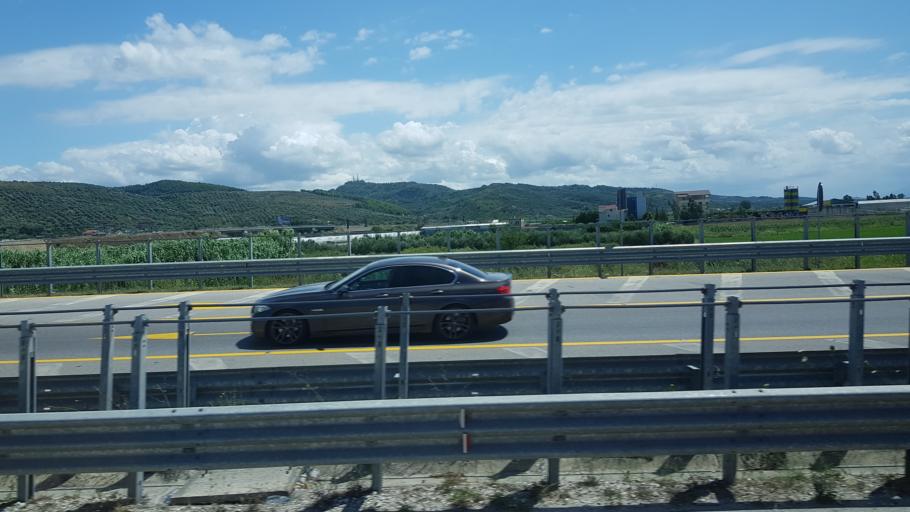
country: AL
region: Fier
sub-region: Rrethi i Fierit
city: Levan
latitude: 40.6695
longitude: 19.4785
